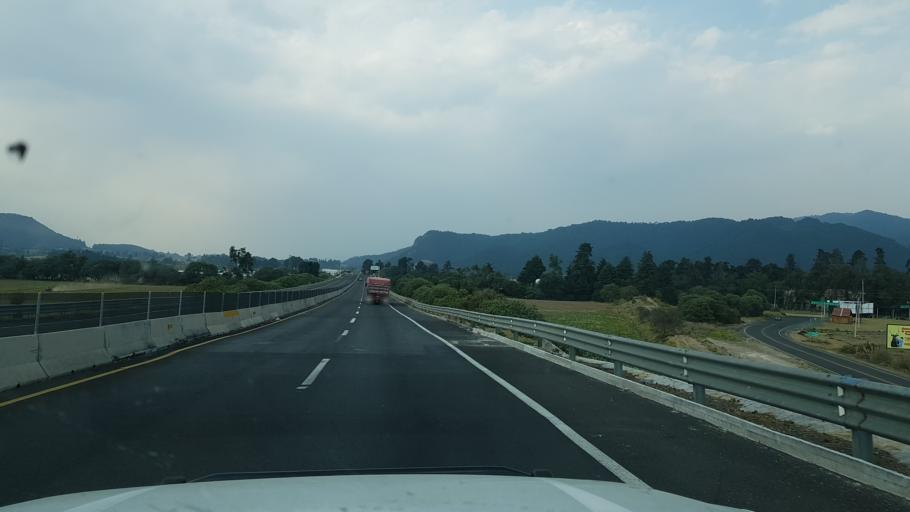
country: MX
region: Mexico
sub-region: Ayapango
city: La Colonia
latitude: 19.1401
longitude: -98.7761
